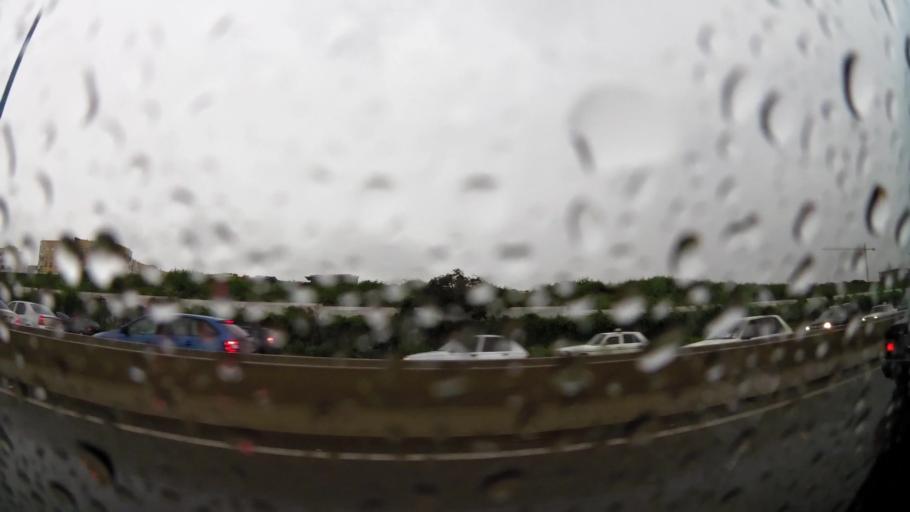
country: MA
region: Grand Casablanca
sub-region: Mediouna
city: Tit Mellil
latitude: 33.5931
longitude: -7.5246
